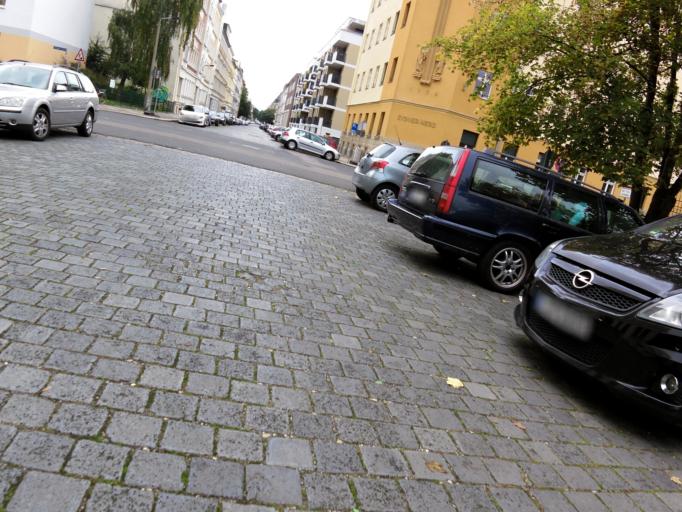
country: DE
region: Saxony
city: Leipzig
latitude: 51.3220
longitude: 12.3821
